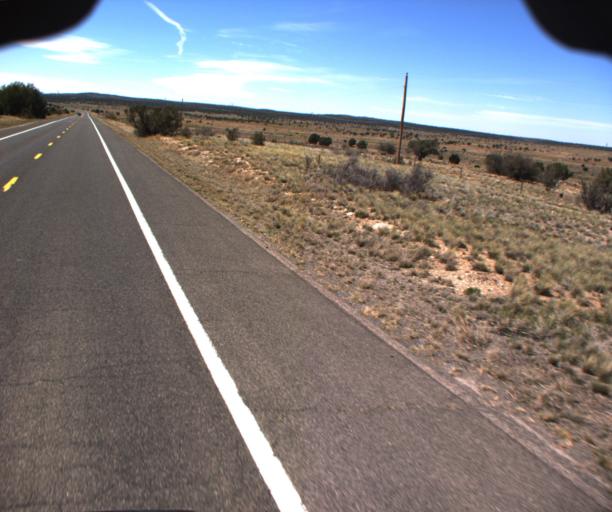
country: US
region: Arizona
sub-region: Mohave County
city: Peach Springs
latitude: 35.5507
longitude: -113.3074
